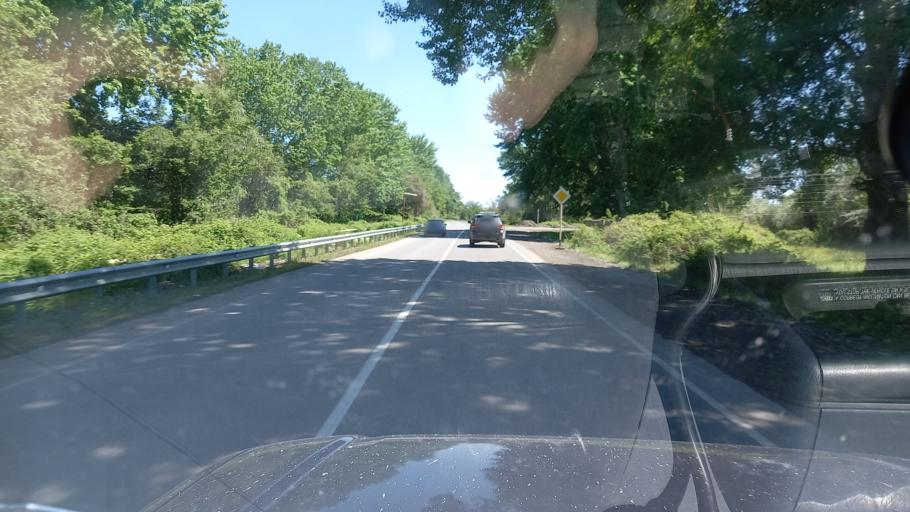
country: RU
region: Dagestan
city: Samur
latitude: 41.7380
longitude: 48.4782
